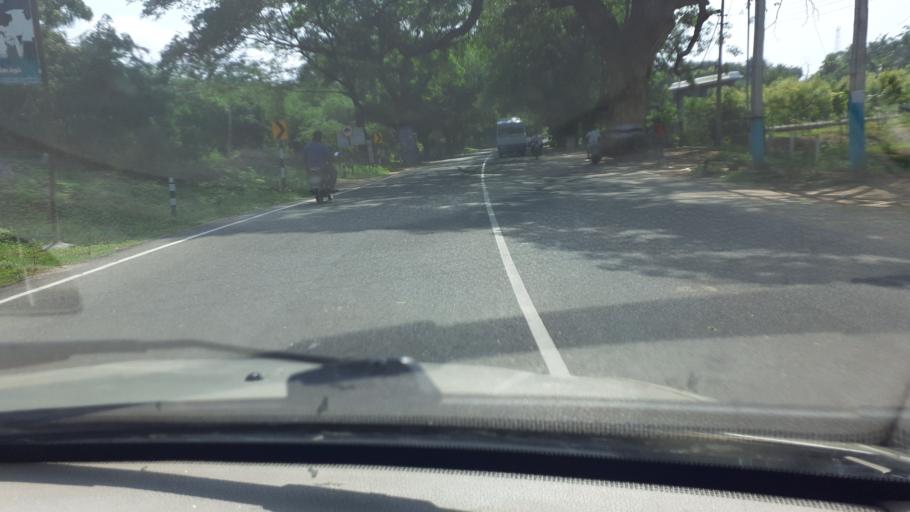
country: IN
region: Tamil Nadu
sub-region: Thoothukkudi
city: Srivaikuntam
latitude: 8.6302
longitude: 77.9052
